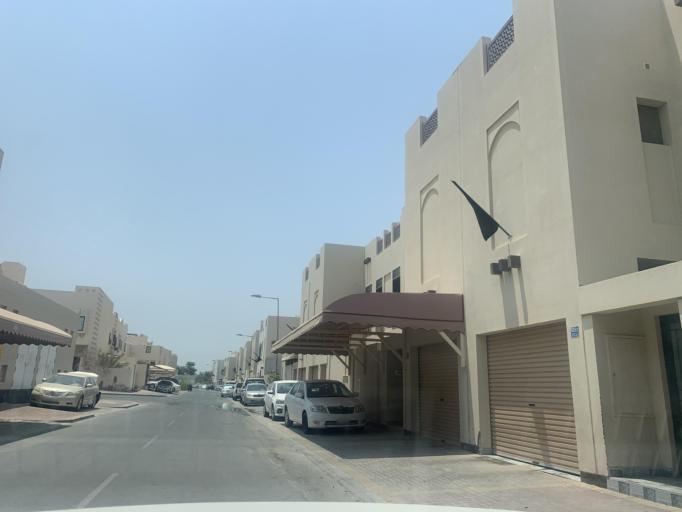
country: BH
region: Central Governorate
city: Madinat Hamad
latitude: 26.1463
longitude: 50.4616
